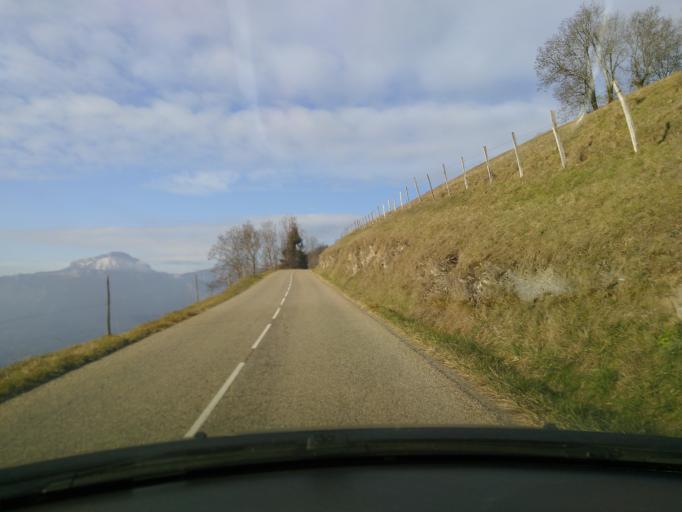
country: FR
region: Rhone-Alpes
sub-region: Departement de l'Isere
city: Froges
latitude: 45.2344
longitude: 5.9317
